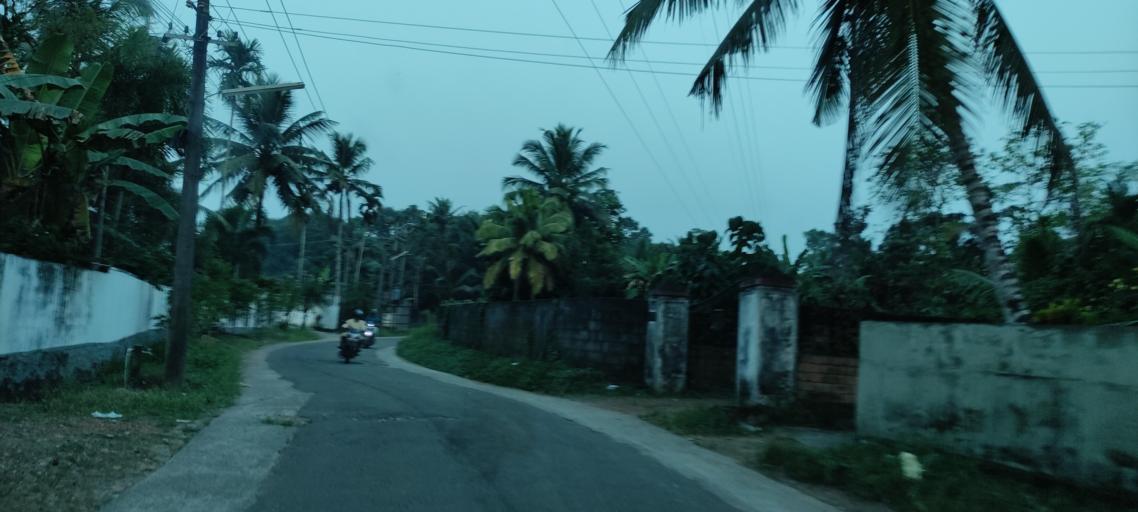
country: IN
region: Kerala
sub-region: Pattanamtitta
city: Adur
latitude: 9.1601
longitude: 76.7407
